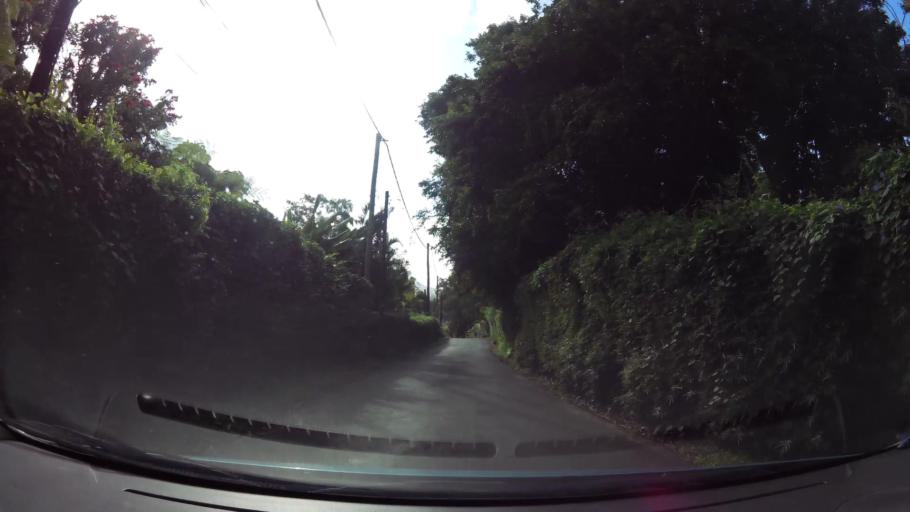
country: MU
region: Plaines Wilhems
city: Curepipe
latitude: -20.3165
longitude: 57.4997
